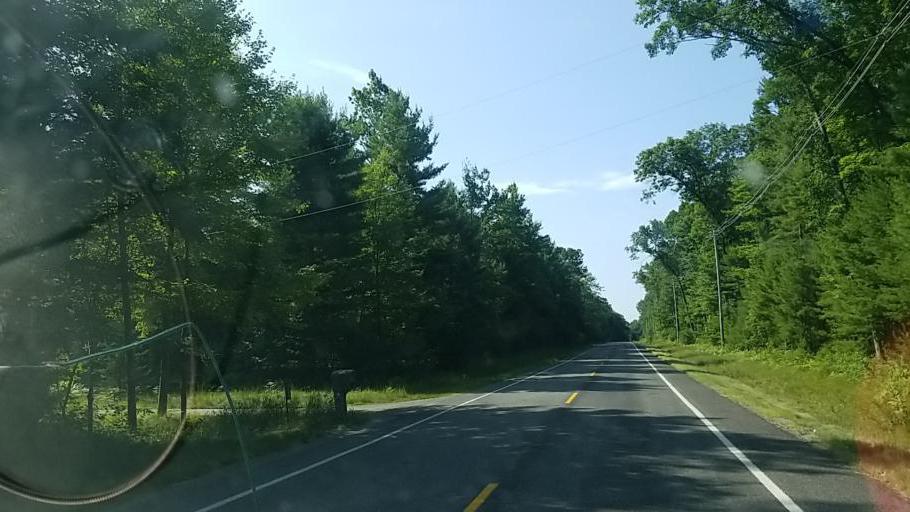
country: US
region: Michigan
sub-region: Muskegon County
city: Whitehall
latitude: 43.3508
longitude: -86.3764
